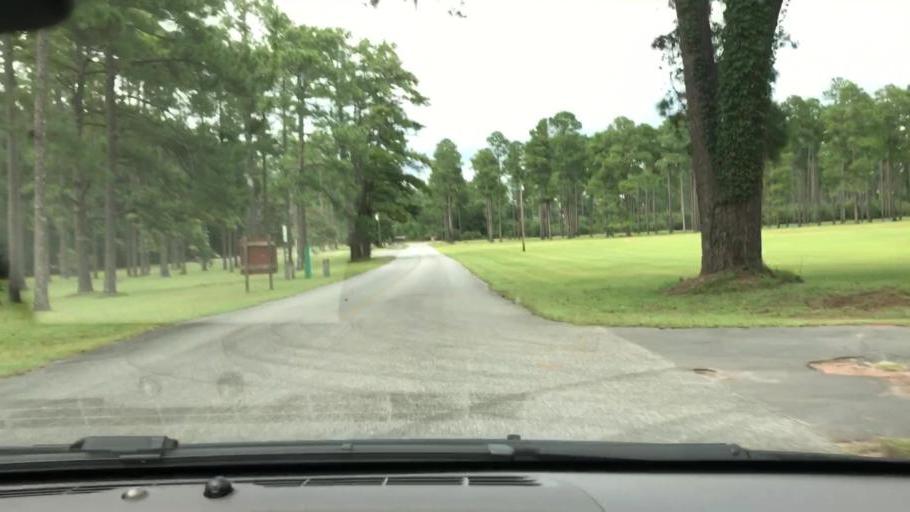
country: US
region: Georgia
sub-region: Early County
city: Blakely
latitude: 31.4688
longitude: -84.9271
